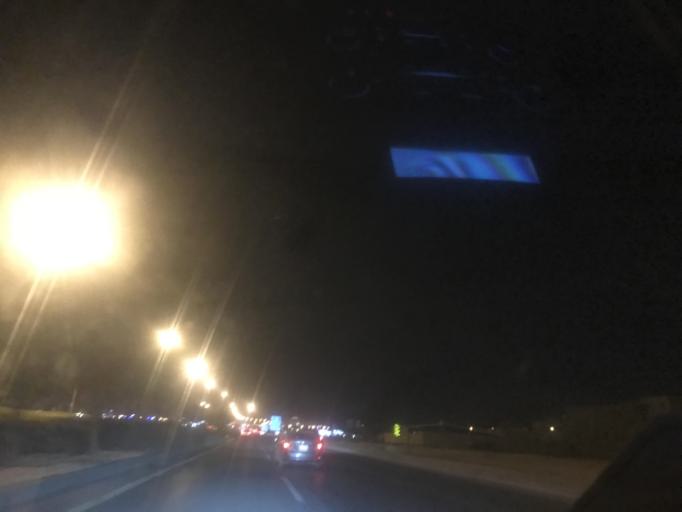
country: SA
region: Ar Riyad
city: Riyadh
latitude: 24.7681
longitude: 46.5762
